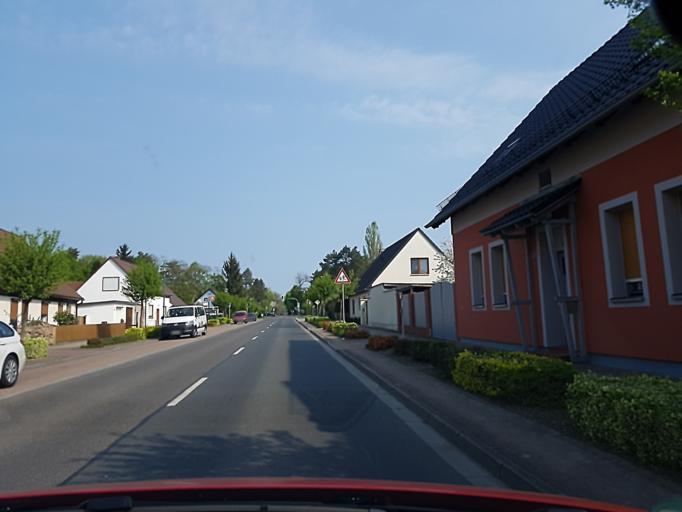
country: DE
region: Saxony
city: Bad Duben
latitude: 51.5963
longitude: 12.5848
